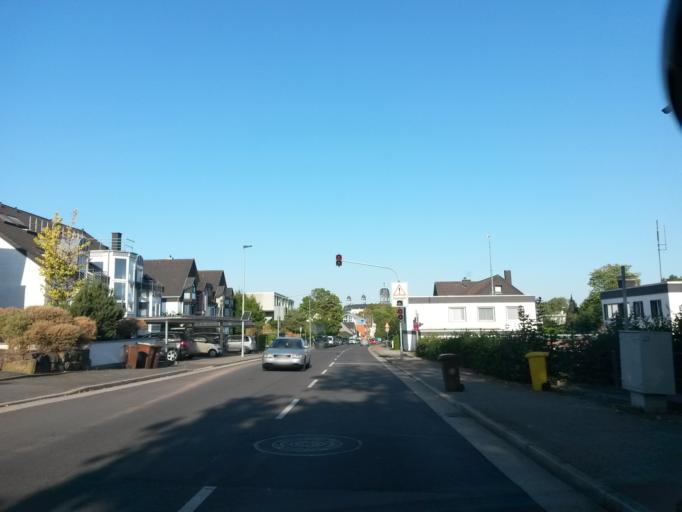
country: DE
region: North Rhine-Westphalia
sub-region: Regierungsbezirk Koln
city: Bergisch Gladbach
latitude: 50.9666
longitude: 7.1690
